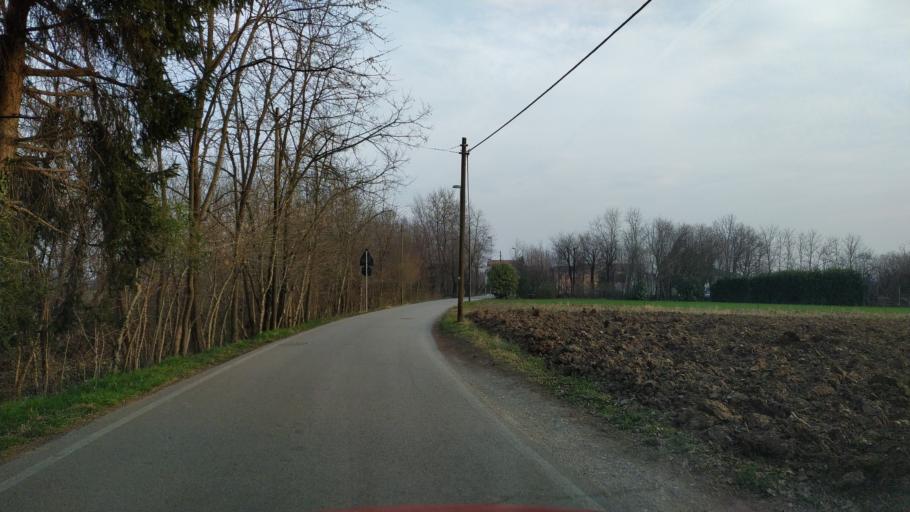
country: IT
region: Veneto
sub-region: Provincia di Vicenza
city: Marano Vicentino
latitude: 45.6807
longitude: 11.4361
